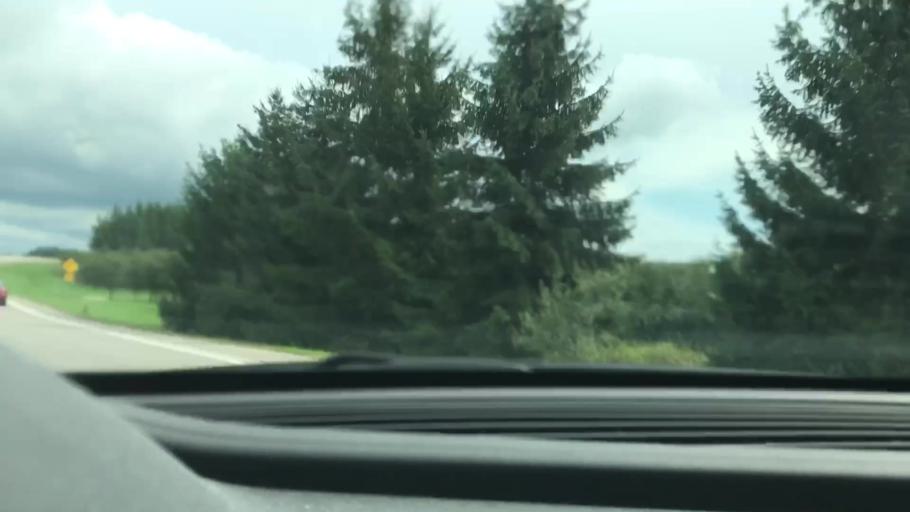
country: US
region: Michigan
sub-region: Antrim County
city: Bellaire
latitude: 45.0989
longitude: -85.3049
